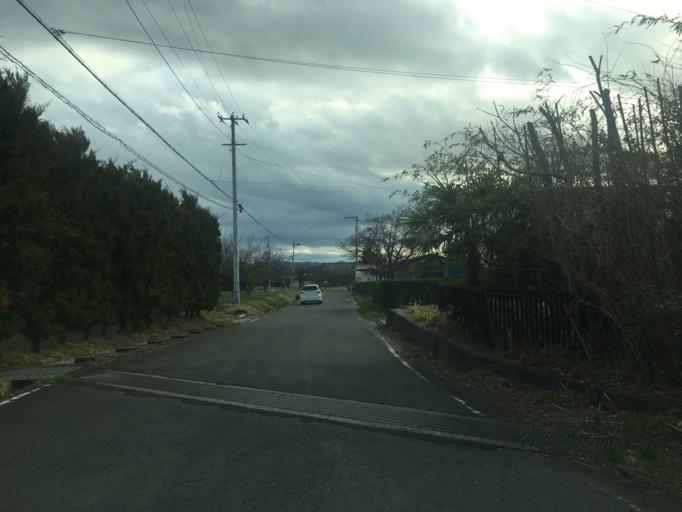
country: JP
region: Fukushima
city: Yanagawamachi-saiwaicho
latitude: 37.8819
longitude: 140.5750
